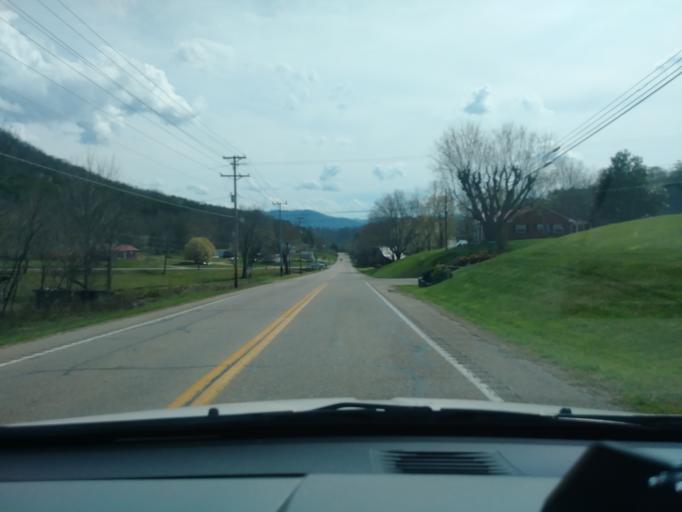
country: US
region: Tennessee
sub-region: Greene County
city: Greeneville
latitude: 36.0449
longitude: -82.8569
